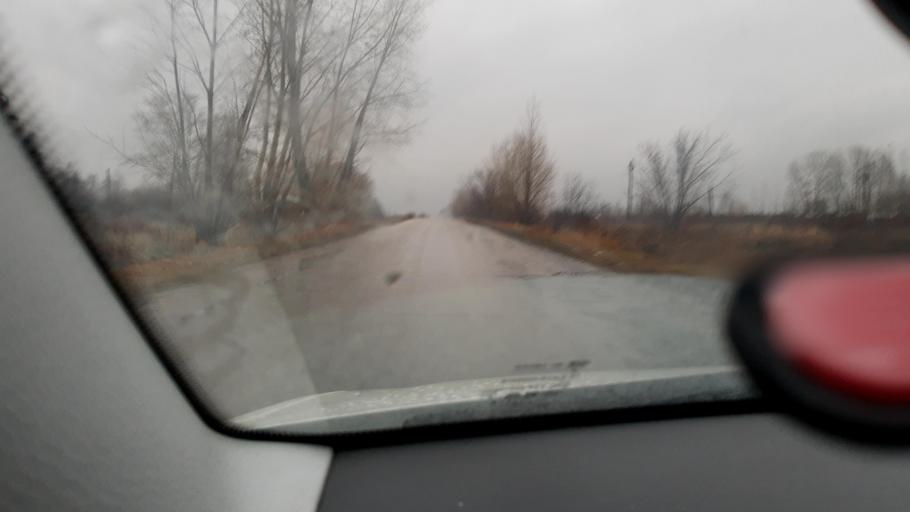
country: RU
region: Bashkortostan
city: Ufa
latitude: 54.8818
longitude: 56.1334
